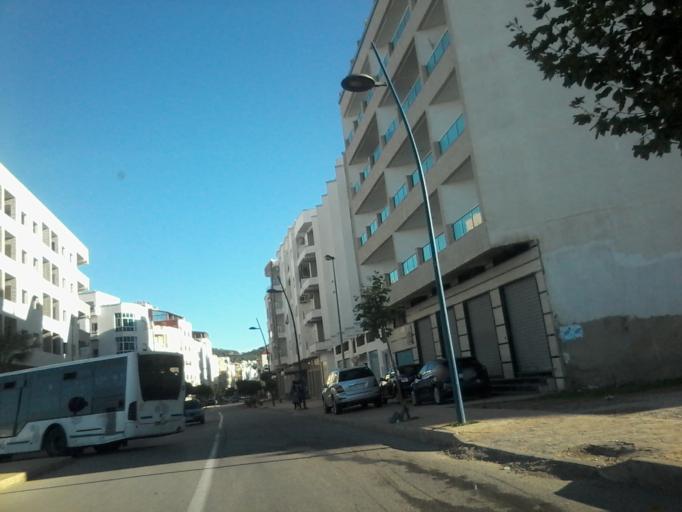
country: MA
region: Tanger-Tetouan
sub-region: Tetouan
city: Martil
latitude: 35.6882
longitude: -5.3274
